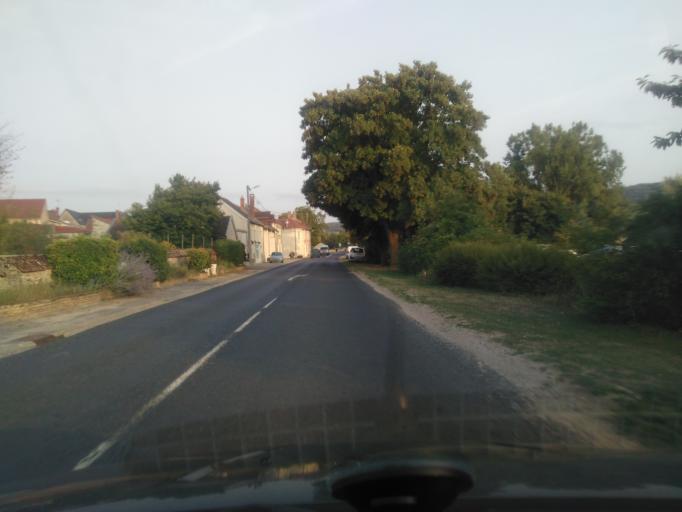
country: FR
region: Champagne-Ardenne
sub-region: Departement de la Marne
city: Mareuil-le-Port
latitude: 49.0833
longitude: 3.7966
